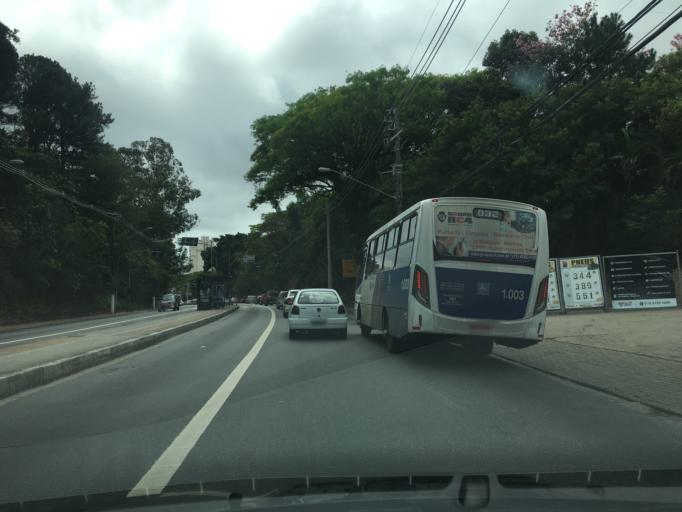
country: BR
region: Sao Paulo
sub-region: Taboao Da Serra
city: Taboao da Serra
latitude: -23.6052
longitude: -46.7462
